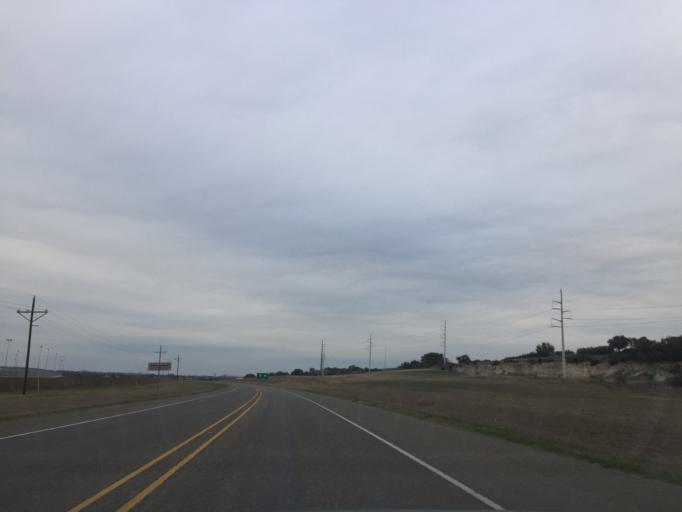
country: US
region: Texas
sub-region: Coryell County
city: Gatesville
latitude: 31.4747
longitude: -97.7207
